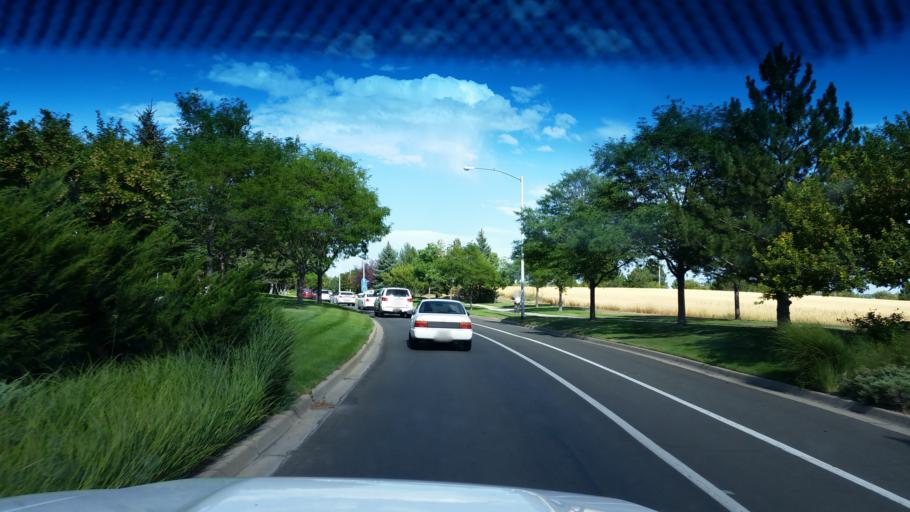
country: US
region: Colorado
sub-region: Broomfield County
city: Broomfield
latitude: 39.9242
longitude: -105.0681
